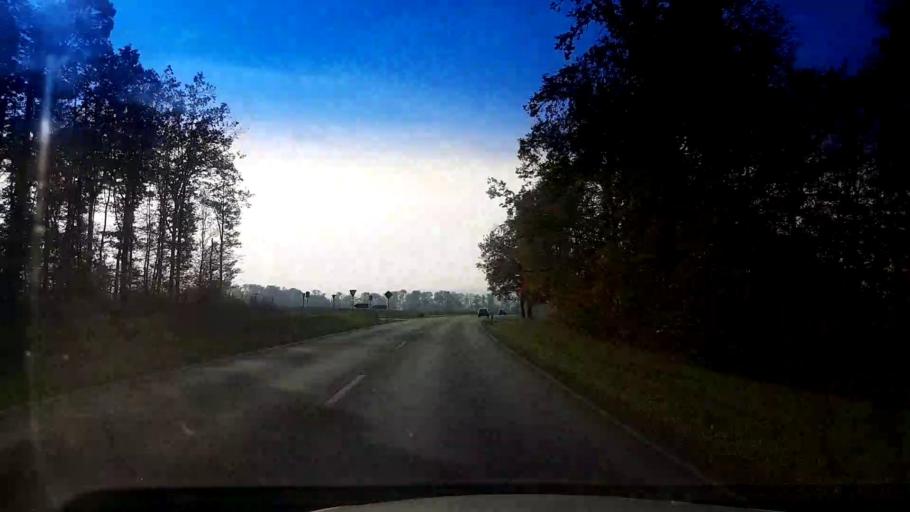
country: DE
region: Bavaria
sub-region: Upper Franconia
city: Himmelkron
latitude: 50.0764
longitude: 11.6096
